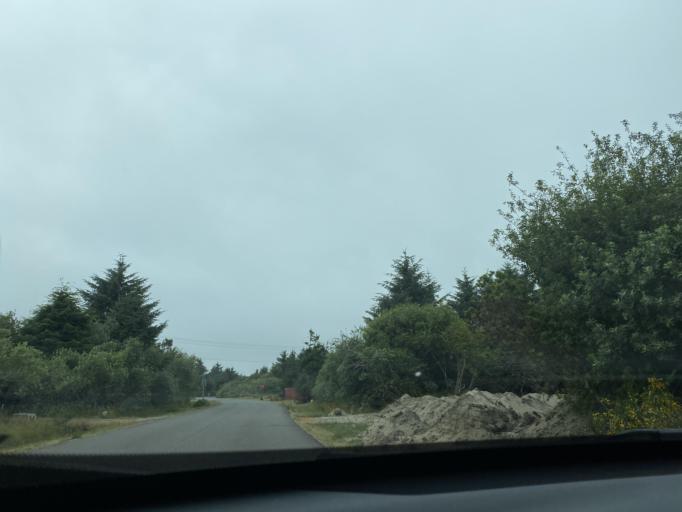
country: US
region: Washington
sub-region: Grays Harbor County
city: Ocean Shores
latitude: 46.9518
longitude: -124.1445
